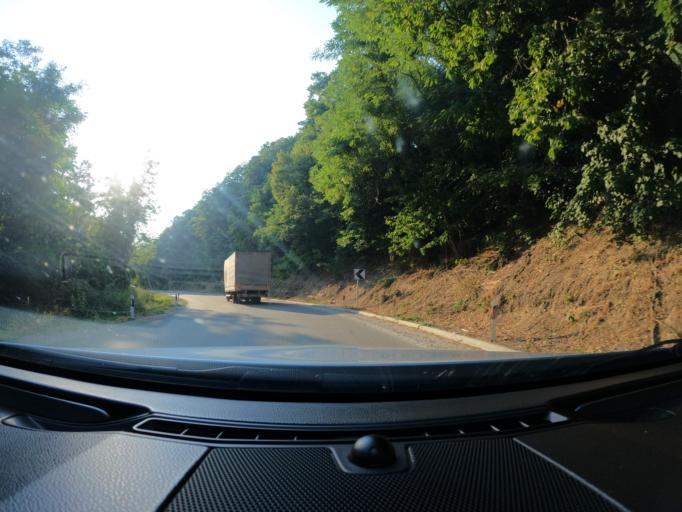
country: RS
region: Autonomna Pokrajina Vojvodina
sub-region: Juznobacki Okrug
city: Beocin
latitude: 45.1430
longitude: 19.7202
